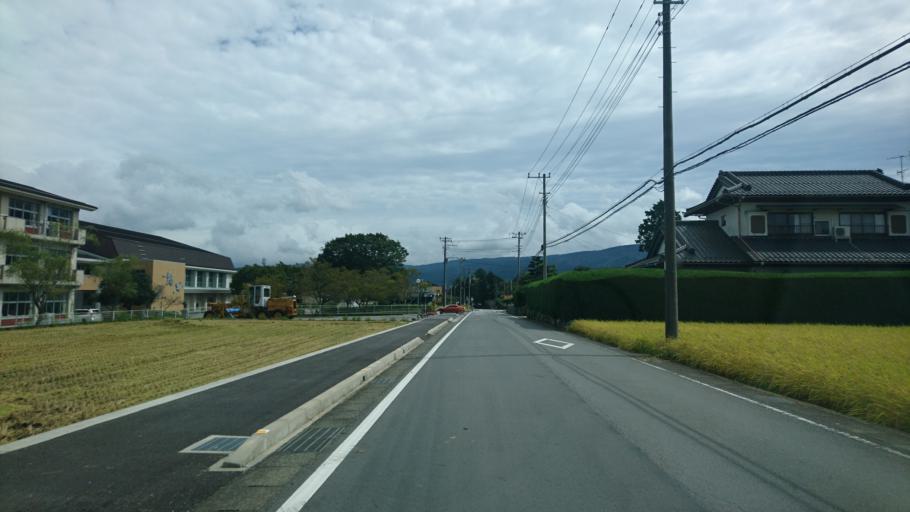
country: JP
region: Shizuoka
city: Gotemba
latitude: 35.3153
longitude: 138.9449
